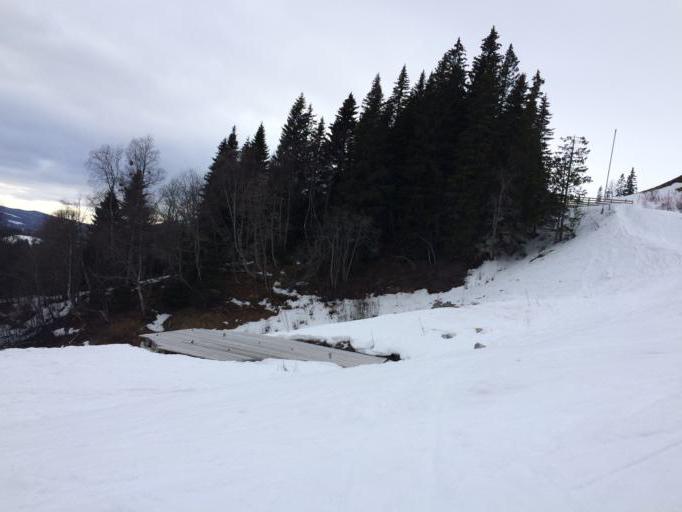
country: SE
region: Jaemtland
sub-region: Are Kommun
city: Are
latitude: 63.4067
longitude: 13.0569
